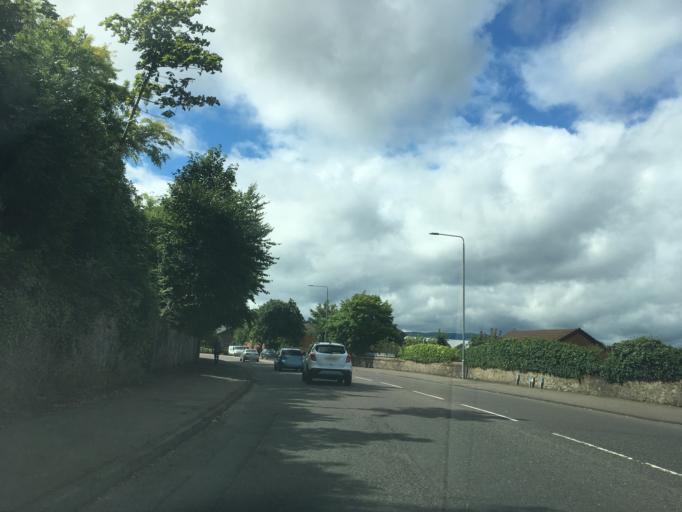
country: GB
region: Scotland
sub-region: Inverclyde
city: Gourock
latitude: 55.9620
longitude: -4.7922
